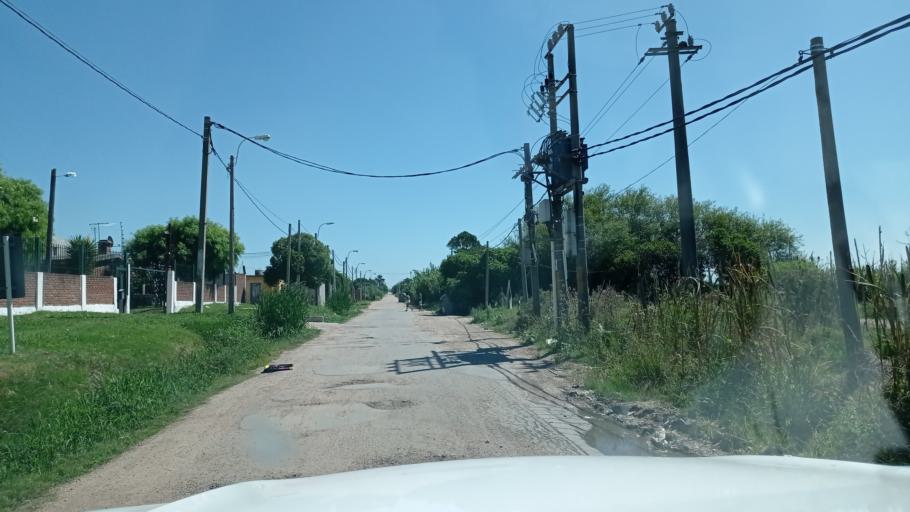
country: UY
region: Montevideo
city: Montevideo
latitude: -34.8690
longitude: -56.2717
